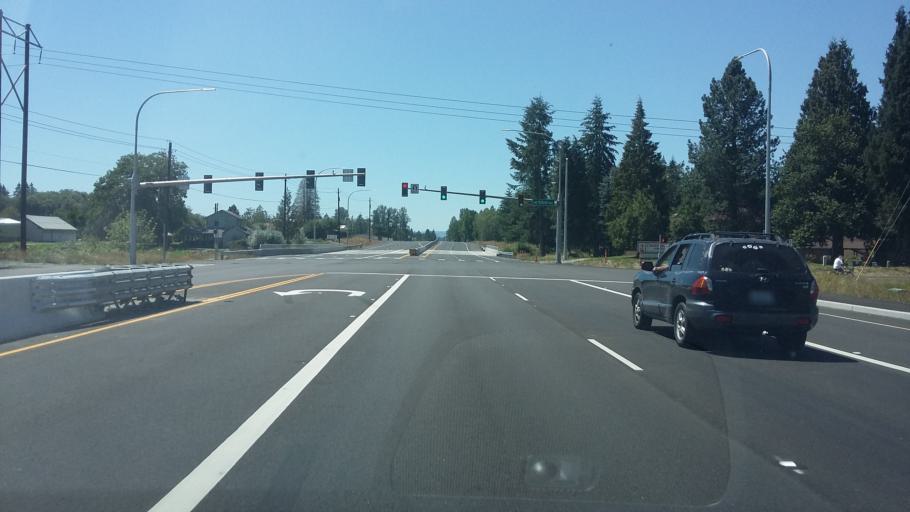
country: US
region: Washington
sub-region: Clark County
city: Dollar Corner
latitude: 45.7804
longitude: -122.5784
